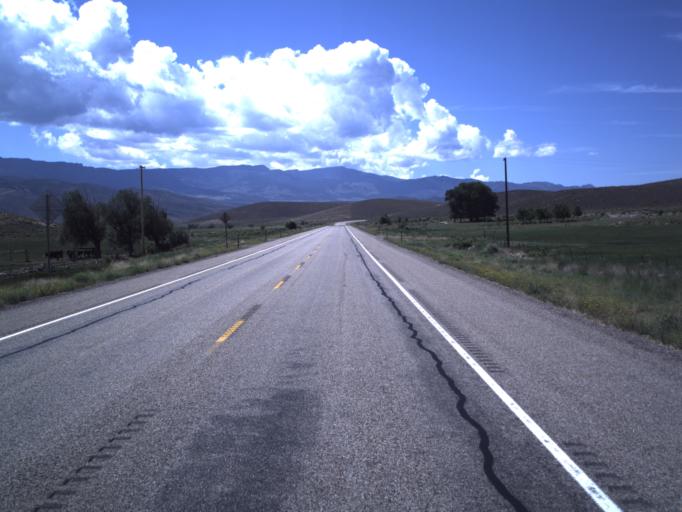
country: US
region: Utah
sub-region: Piute County
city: Junction
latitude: 38.2277
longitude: -112.2198
